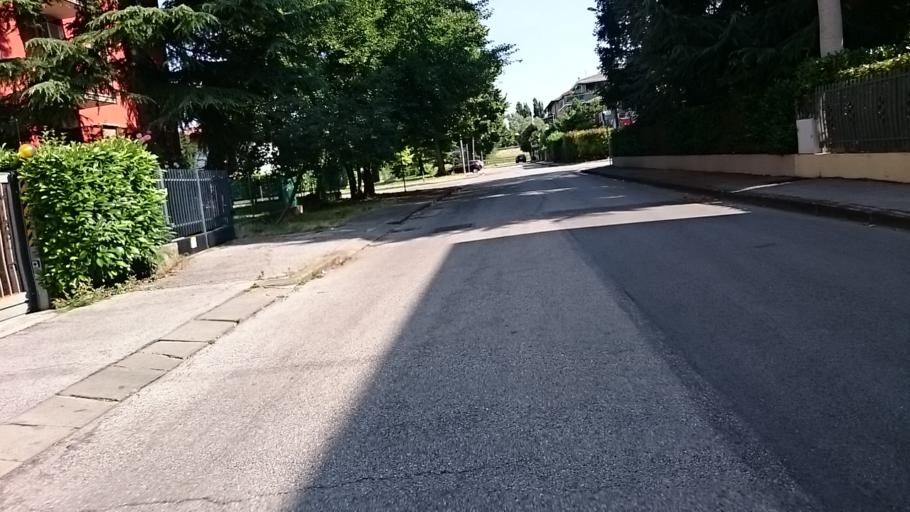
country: IT
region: Veneto
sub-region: Provincia di Padova
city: Mandriola-Sant'Agostino
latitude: 45.3833
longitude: 11.8729
